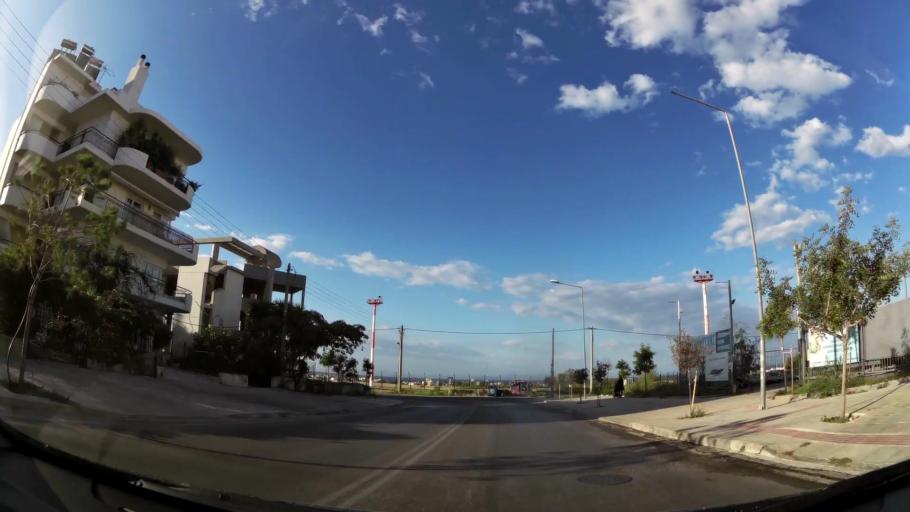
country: GR
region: Attica
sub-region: Nomarchia Athinas
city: Elliniko
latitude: 37.8815
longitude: 23.7438
